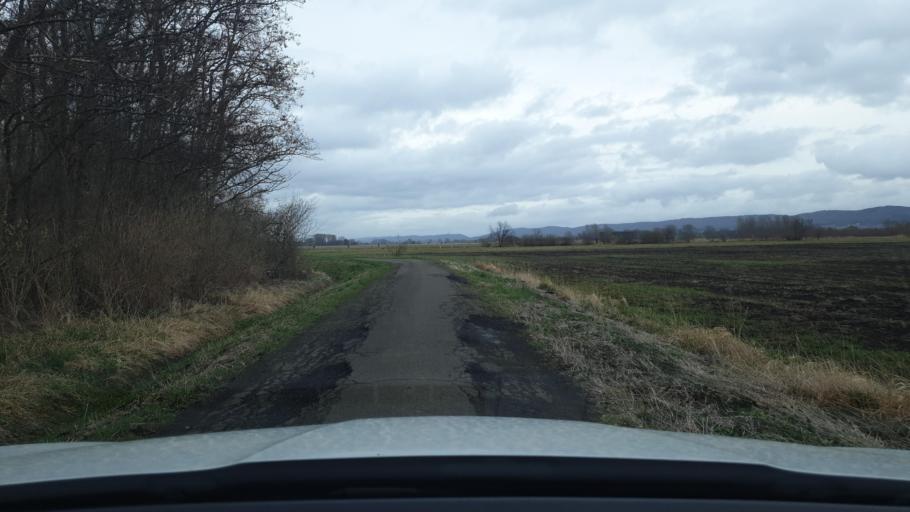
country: DE
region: North Rhine-Westphalia
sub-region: Regierungsbezirk Detmold
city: Hille
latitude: 52.3204
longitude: 8.7486
